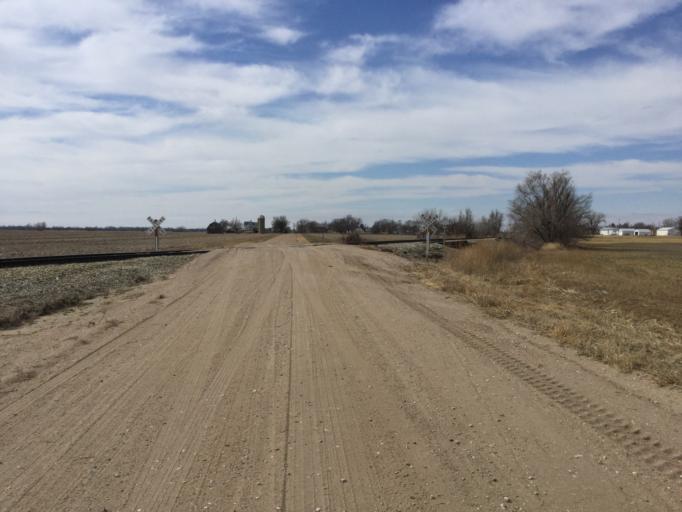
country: US
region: Kansas
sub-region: Barton County
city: Ellinwood
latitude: 38.2748
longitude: -98.4093
